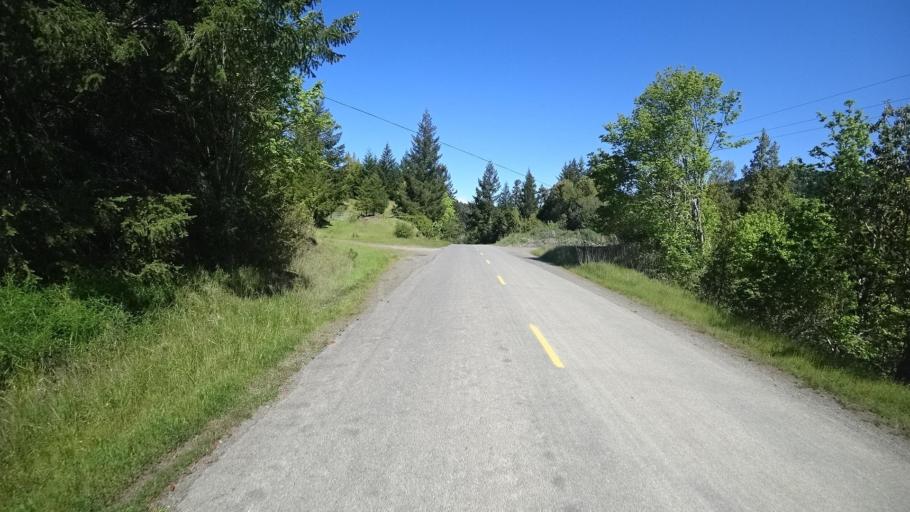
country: US
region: California
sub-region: Humboldt County
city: Rio Dell
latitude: 40.2561
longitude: -124.1913
